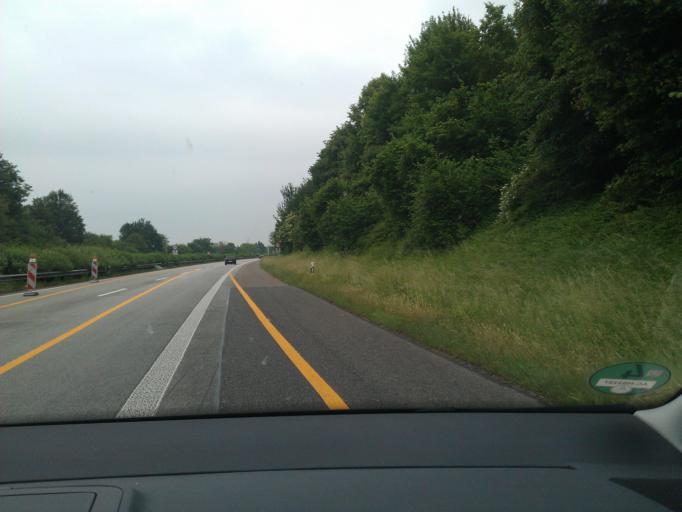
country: DE
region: Rheinland-Pfalz
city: Plaidt
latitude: 50.3770
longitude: 7.4001
